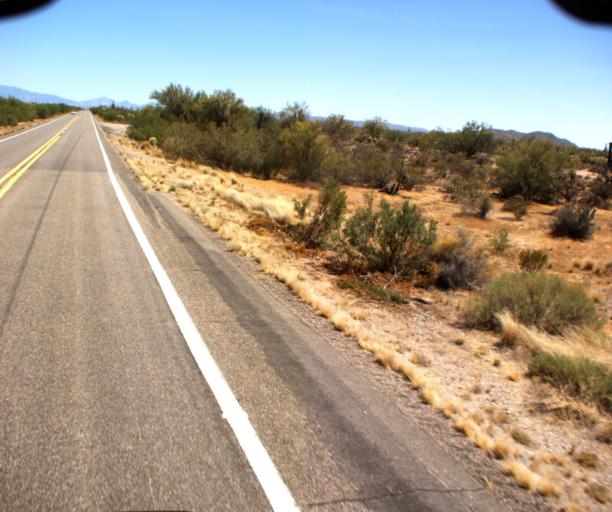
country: US
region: Arizona
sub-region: Pima County
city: Catalina
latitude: 32.7348
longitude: -111.1193
